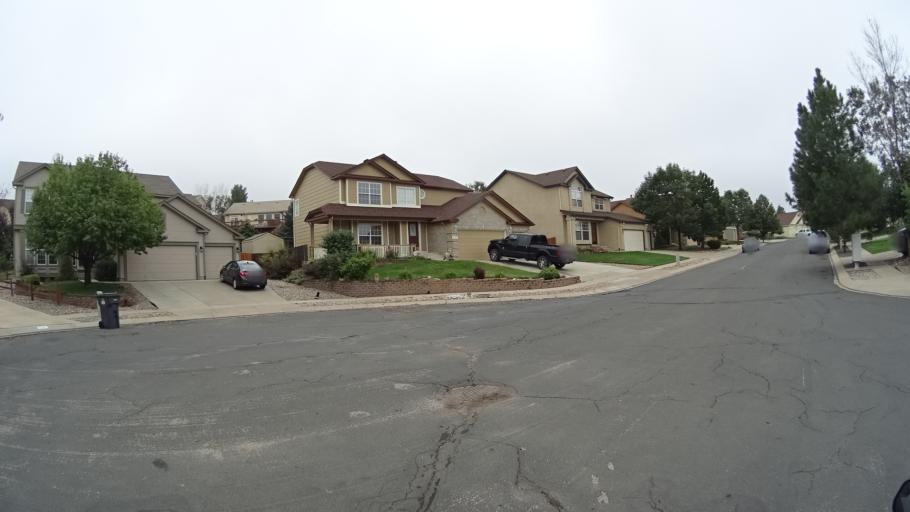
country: US
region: Colorado
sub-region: El Paso County
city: Cimarron Hills
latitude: 38.9325
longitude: -104.7492
